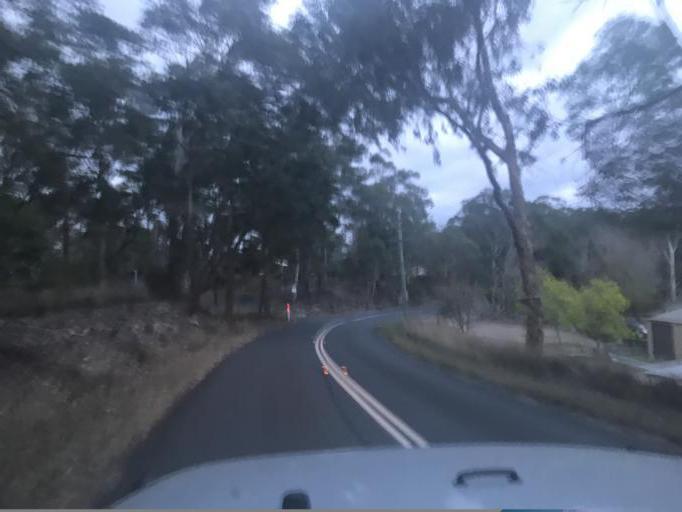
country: AU
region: New South Wales
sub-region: Hawkesbury
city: Pitt Town
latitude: -33.5040
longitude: 150.8647
